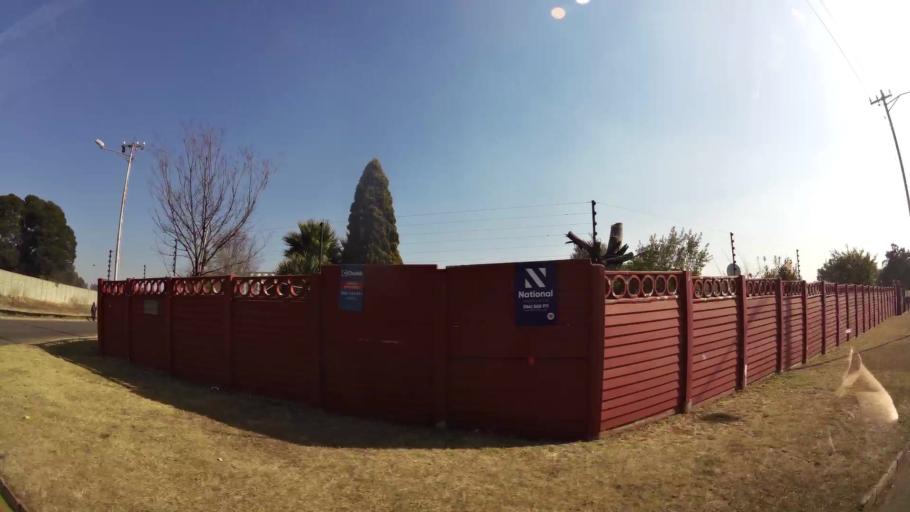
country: ZA
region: Gauteng
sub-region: West Rand District Municipality
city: Randfontein
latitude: -26.1816
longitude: 27.6960
